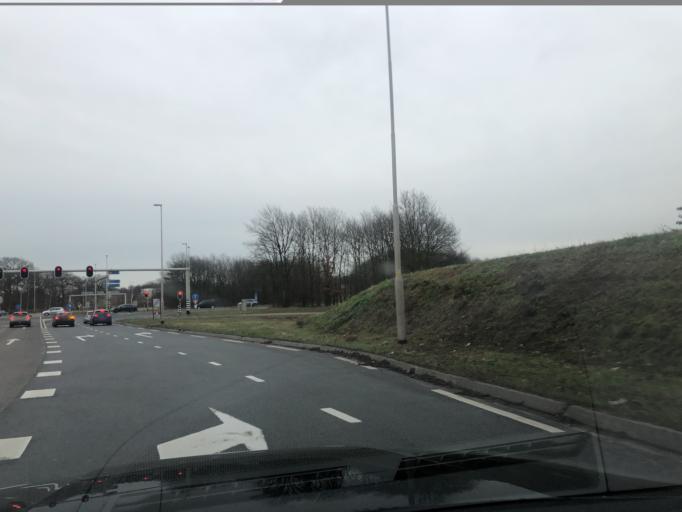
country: NL
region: North Brabant
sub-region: Gemeente Oss
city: Berghem
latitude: 51.7312
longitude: 5.5713
